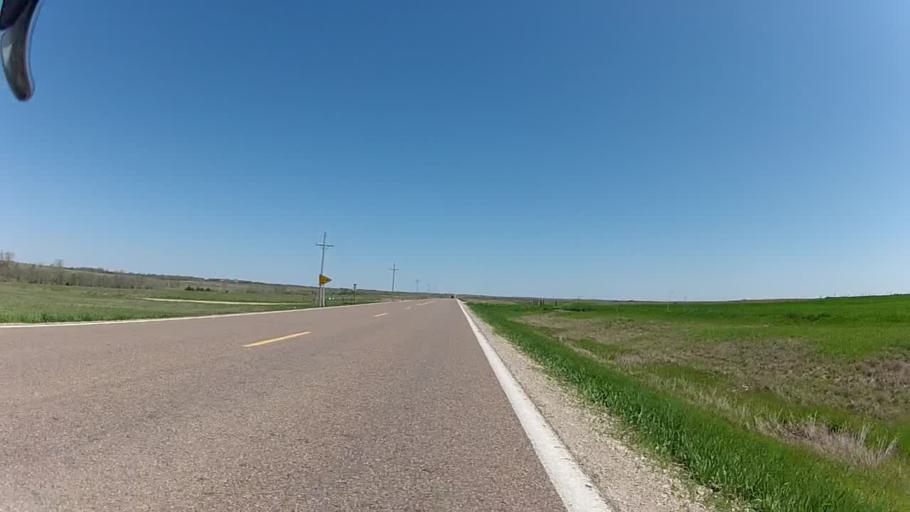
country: US
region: Kansas
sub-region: Morris County
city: Council Grove
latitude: 38.8982
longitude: -96.5201
